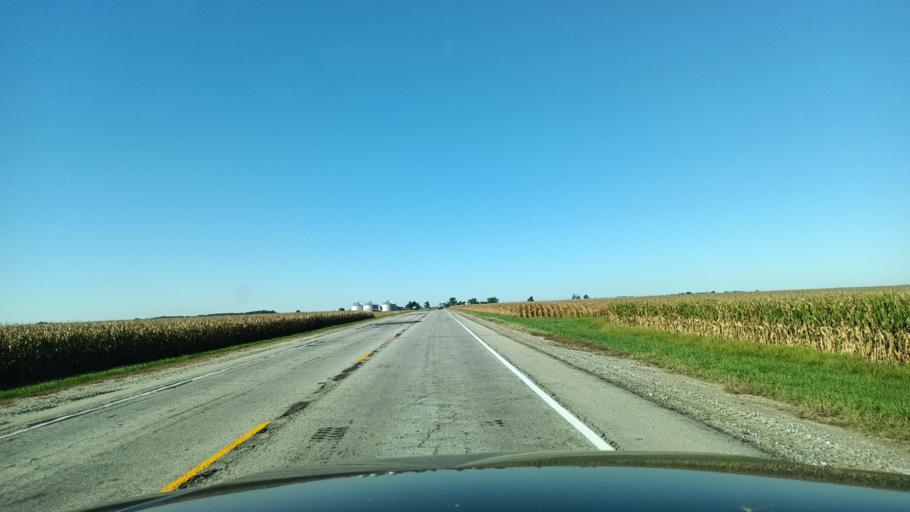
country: US
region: Illinois
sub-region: Warren County
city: Monmouth
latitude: 40.8858
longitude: -90.6746
